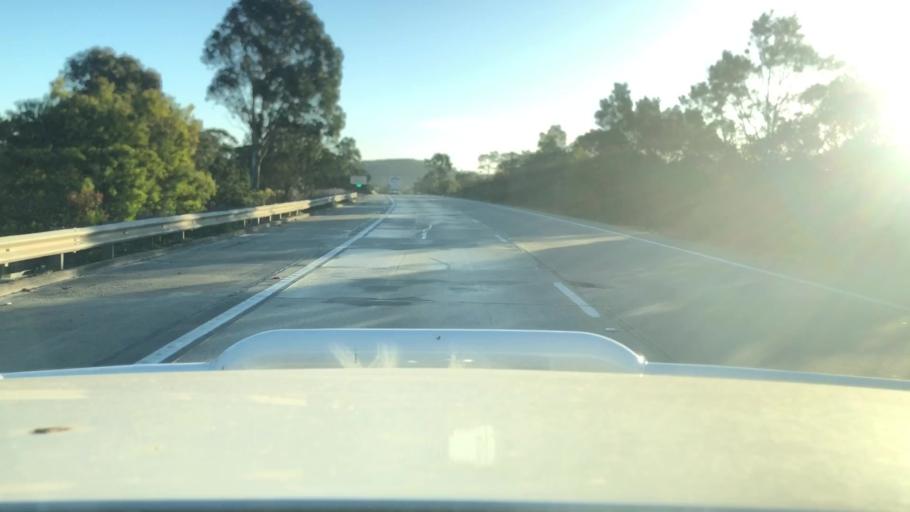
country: AU
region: New South Wales
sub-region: Goulburn Mulwaree
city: Goulburn
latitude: -34.7121
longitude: 150.0093
